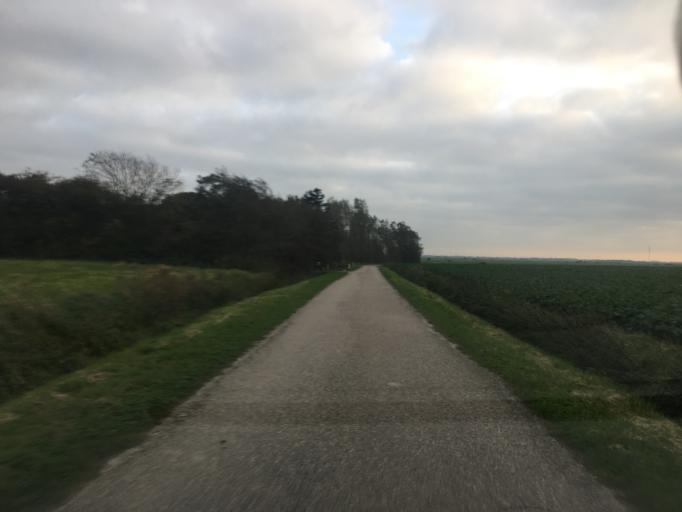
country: DE
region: Schleswig-Holstein
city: Aventoft
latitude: 54.9455
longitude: 8.7803
